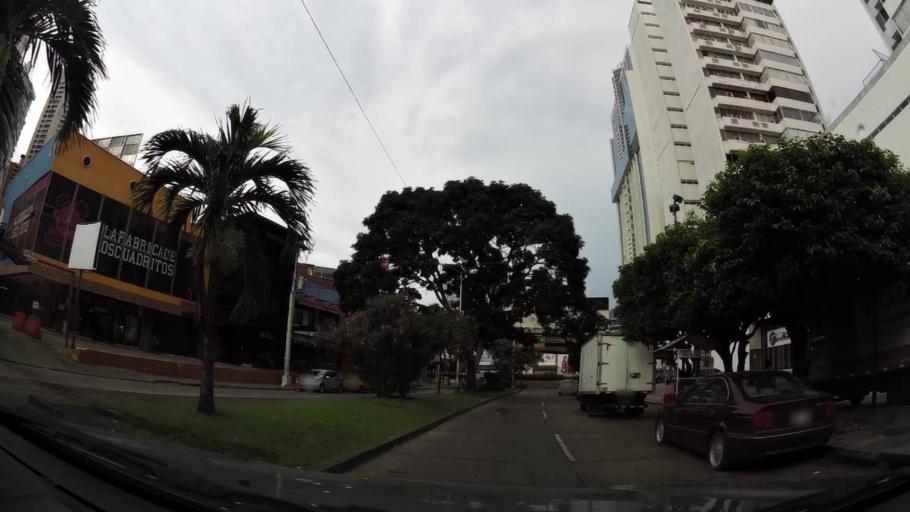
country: PA
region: Panama
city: Panama
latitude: 8.9767
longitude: -79.5153
